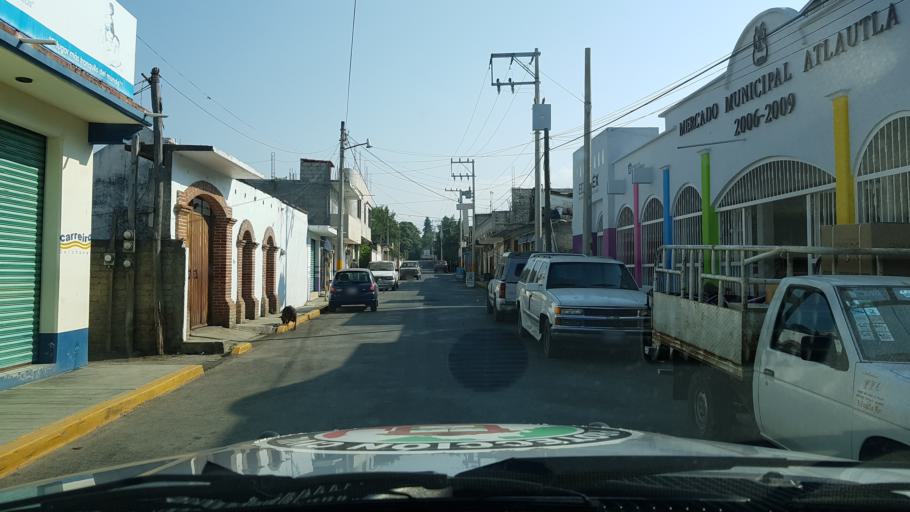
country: MX
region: Mexico
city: Atlautla
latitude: 19.0312
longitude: -98.7821
